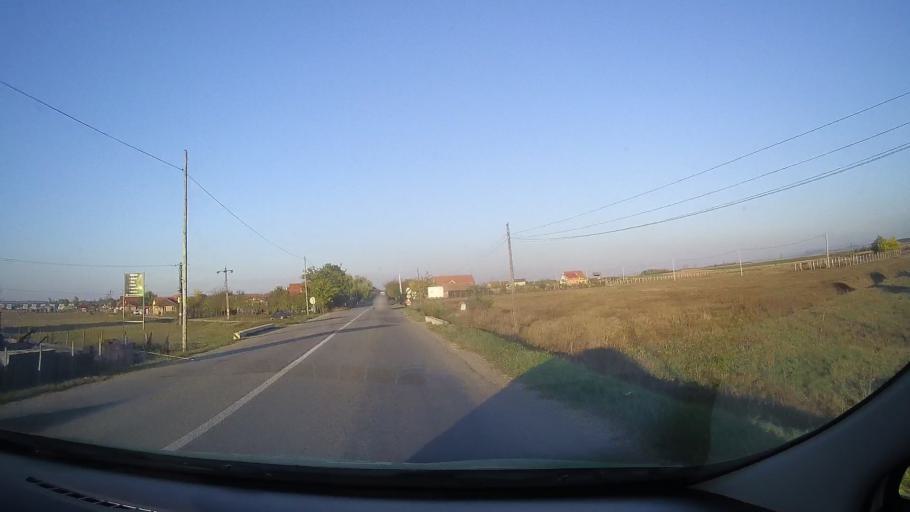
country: RO
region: Bihor
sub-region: Comuna Salard
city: Salard
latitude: 47.2115
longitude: 22.0233
